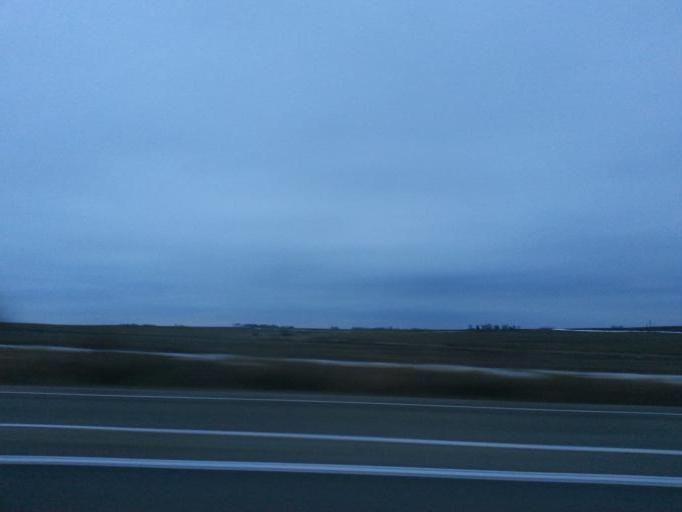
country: US
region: Iowa
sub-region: Buchanan County
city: Jesup
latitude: 42.3521
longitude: -92.0594
